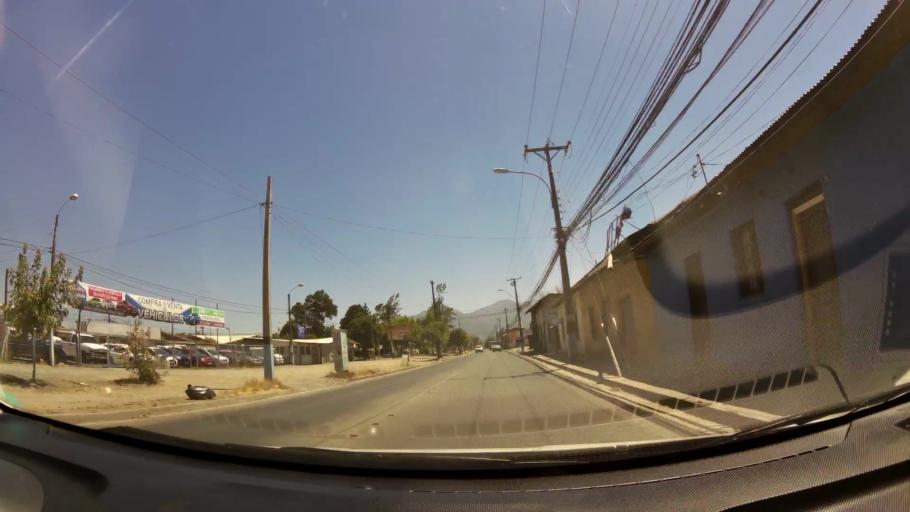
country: CL
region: O'Higgins
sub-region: Provincia de Cachapoal
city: Rancagua
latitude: -34.1668
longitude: -70.7622
